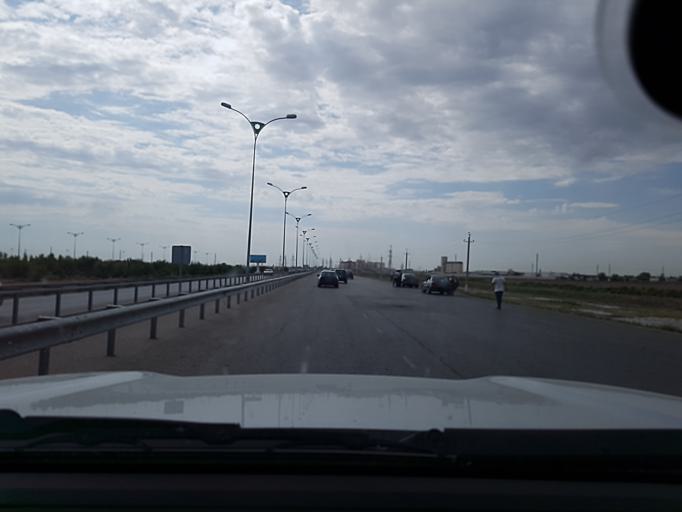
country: TM
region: Dasoguz
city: Dasoguz
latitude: 41.8761
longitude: 59.9472
